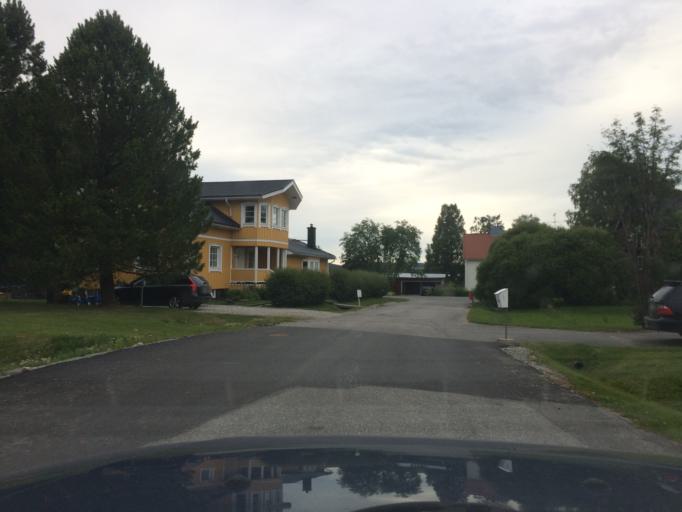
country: SE
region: Norrbotten
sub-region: Pitea Kommun
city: Bergsviken
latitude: 65.3479
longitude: 21.4072
